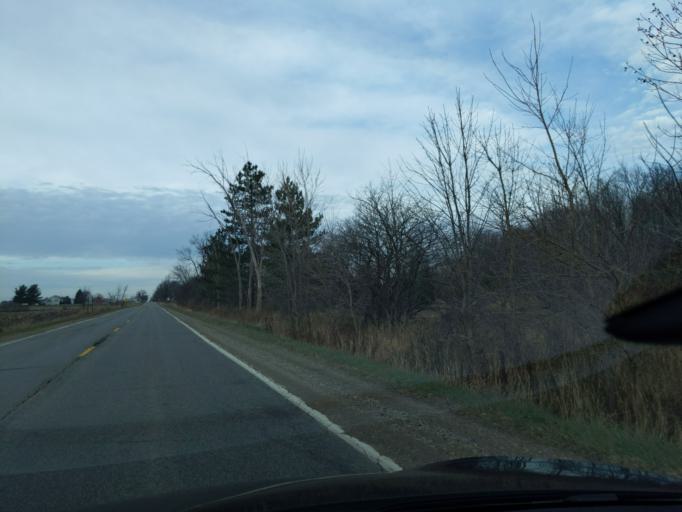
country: US
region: Michigan
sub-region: Ingham County
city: Williamston
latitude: 42.6449
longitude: -84.3638
